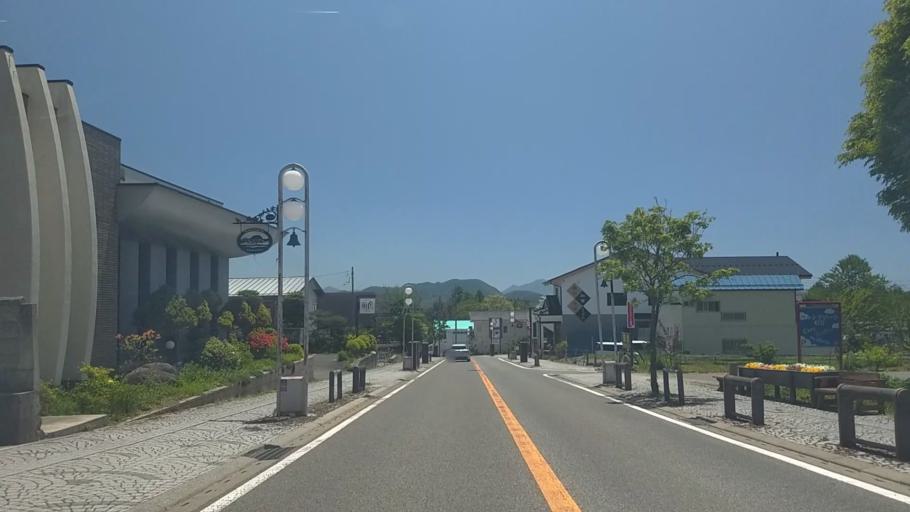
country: JP
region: Yamanashi
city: Nirasaki
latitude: 35.9186
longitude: 138.4380
